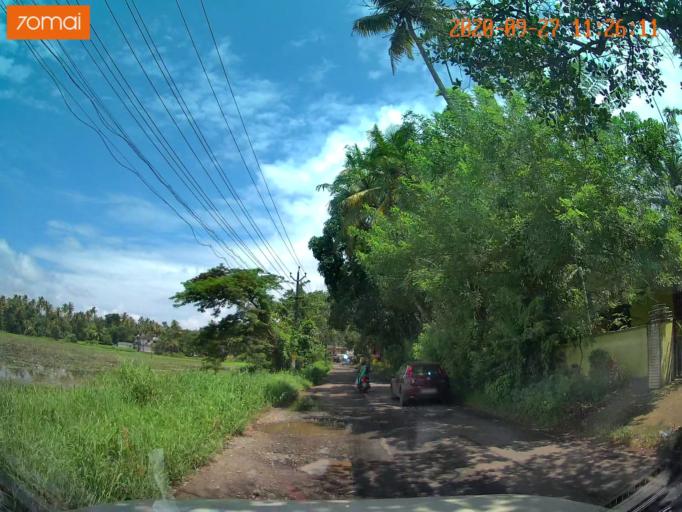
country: IN
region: Kerala
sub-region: Thrissur District
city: Thanniyam
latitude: 10.4148
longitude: 76.1540
